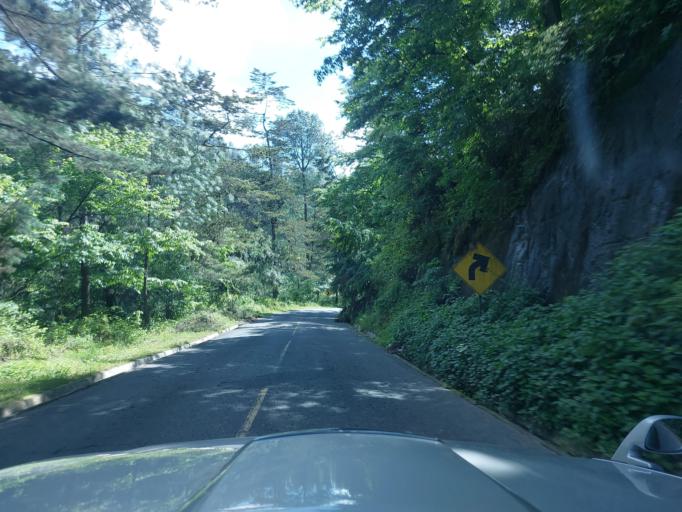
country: GT
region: Chimaltenango
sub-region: Municipio de Santa Cruz Balanya
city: Santa Cruz Balanya
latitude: 14.6948
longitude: -90.8969
